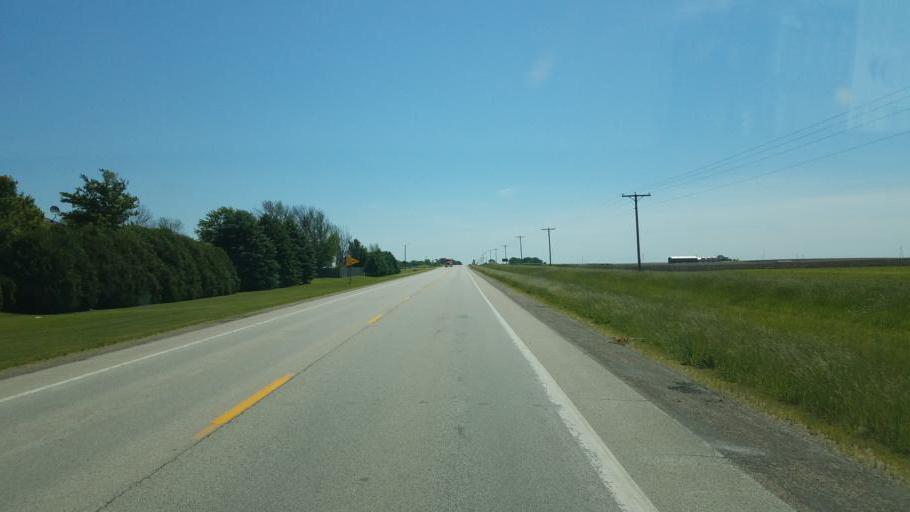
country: US
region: Illinois
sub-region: McLean County
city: Heyworth
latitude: 40.3121
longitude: -88.9679
